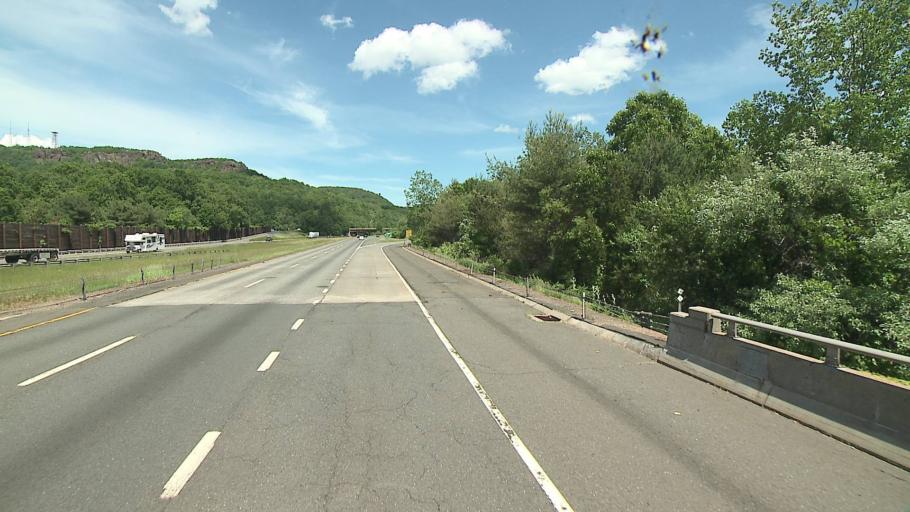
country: US
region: Connecticut
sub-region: New Haven County
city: Meriden
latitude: 41.5539
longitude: -72.8535
